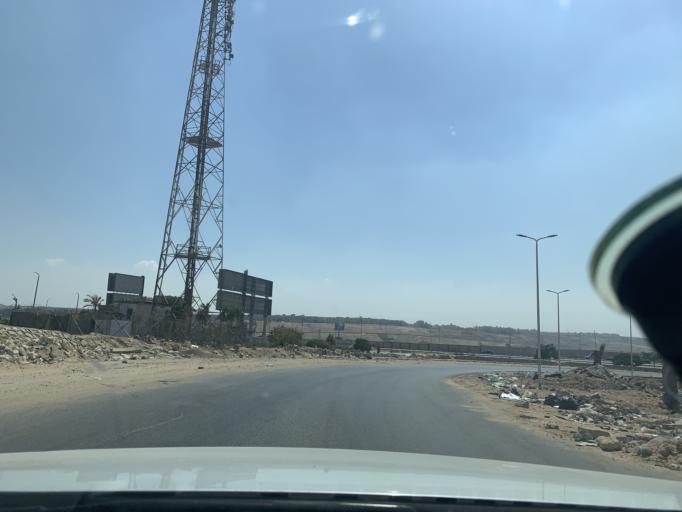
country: EG
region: Muhafazat al Qahirah
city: Cairo
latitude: 30.0242
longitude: 31.3454
